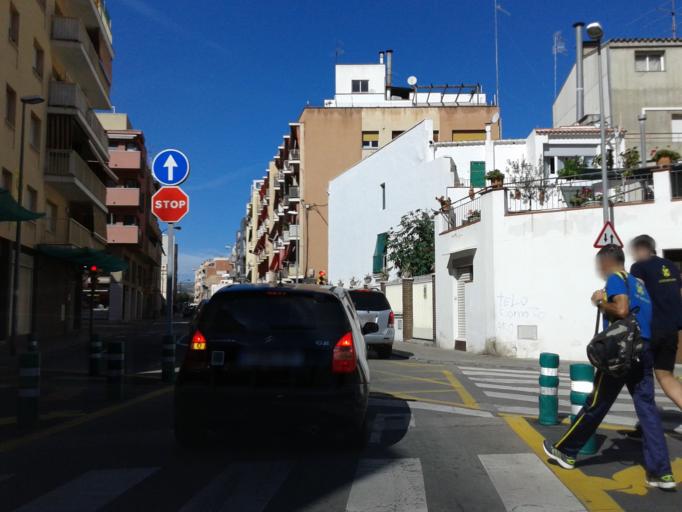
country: ES
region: Catalonia
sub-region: Provincia de Barcelona
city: Vilanova i la Geltru
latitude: 41.2243
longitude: 1.7202
